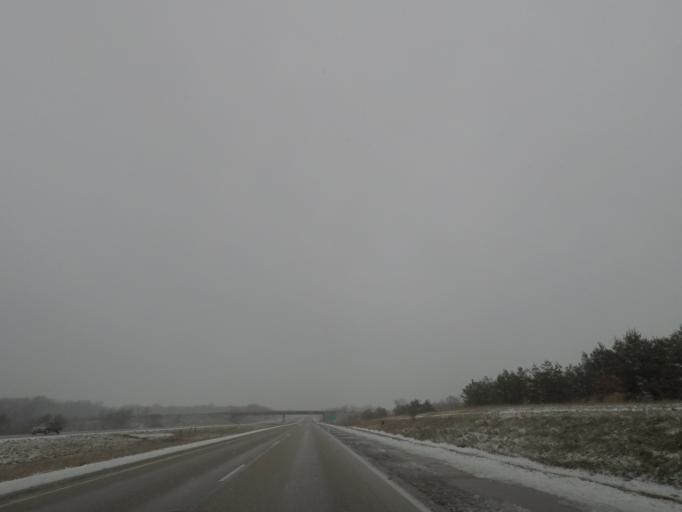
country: US
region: Illinois
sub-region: McLean County
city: Lexington
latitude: 40.6230
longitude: -88.8180
